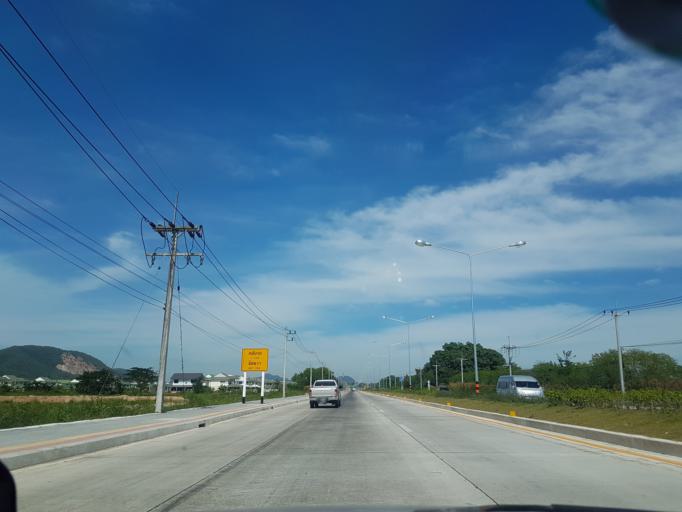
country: TH
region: Chon Buri
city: Sattahip
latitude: 12.6744
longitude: 100.9778
